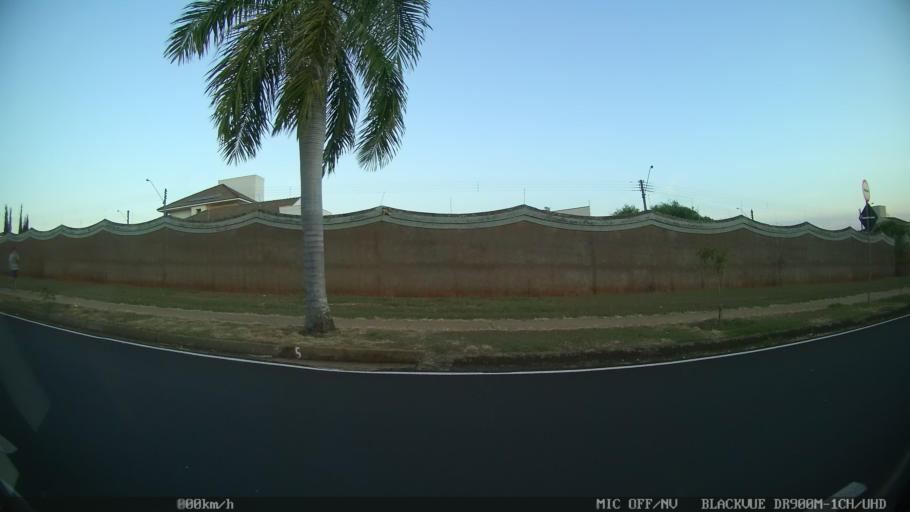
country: BR
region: Sao Paulo
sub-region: Sao Jose Do Rio Preto
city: Sao Jose do Rio Preto
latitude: -20.8165
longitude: -49.3457
